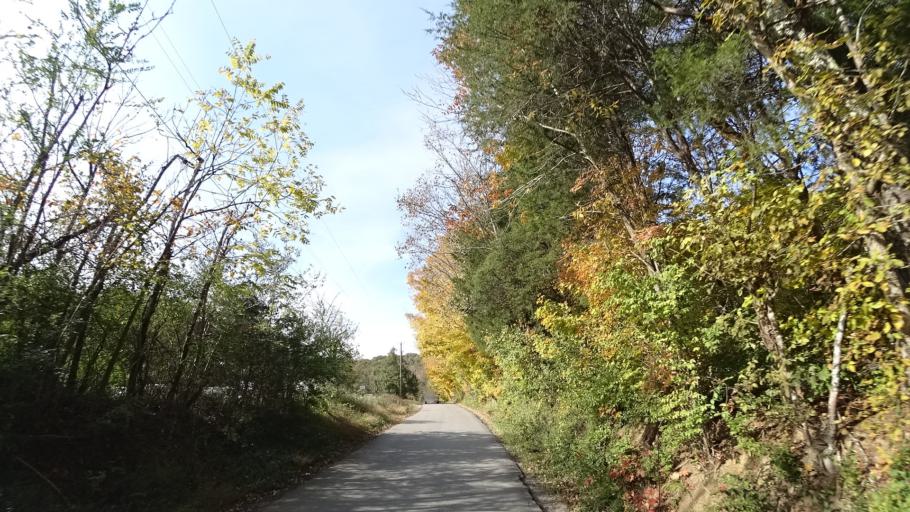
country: US
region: Tennessee
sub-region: Knox County
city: Farragut
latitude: 35.9163
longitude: -84.1775
